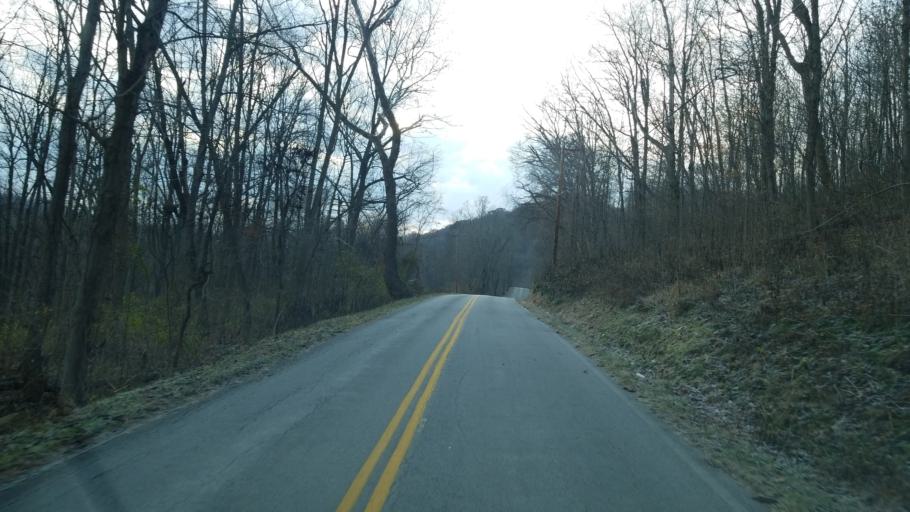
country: US
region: Ohio
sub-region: Ross County
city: Chillicothe
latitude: 39.2333
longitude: -82.8914
